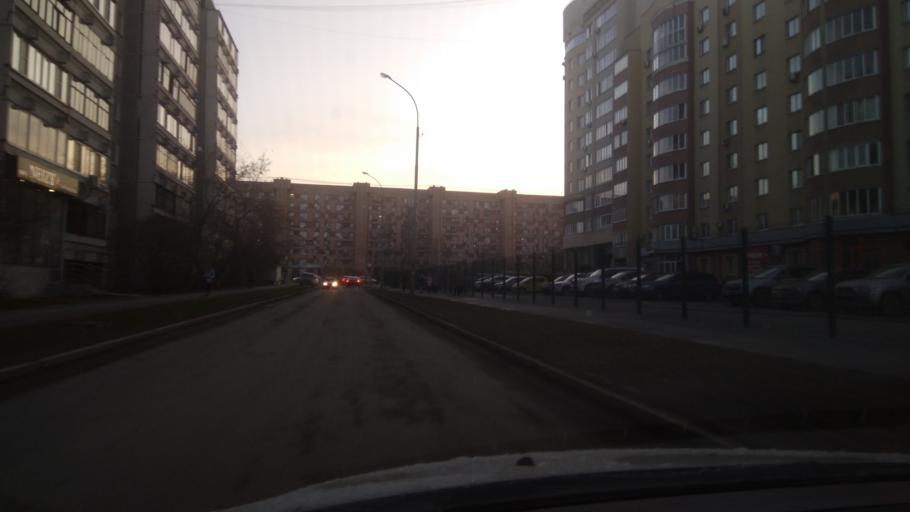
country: RU
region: Sverdlovsk
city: Yekaterinburg
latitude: 56.8374
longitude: 60.5486
